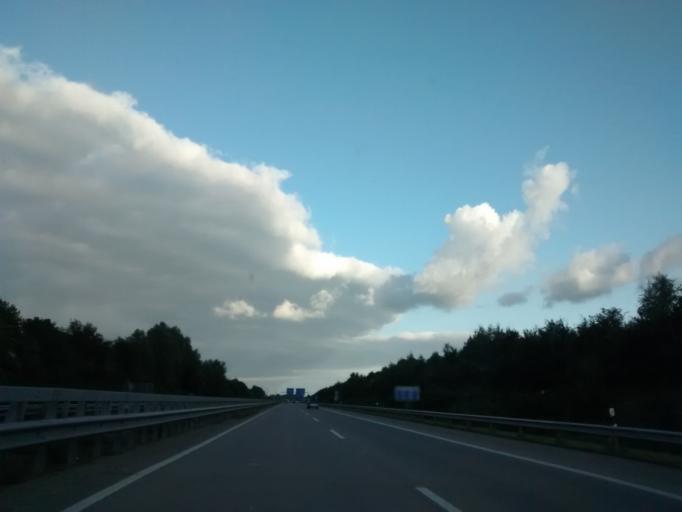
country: DE
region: Lower Saxony
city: Schuttorf
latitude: 52.3428
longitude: 7.2325
